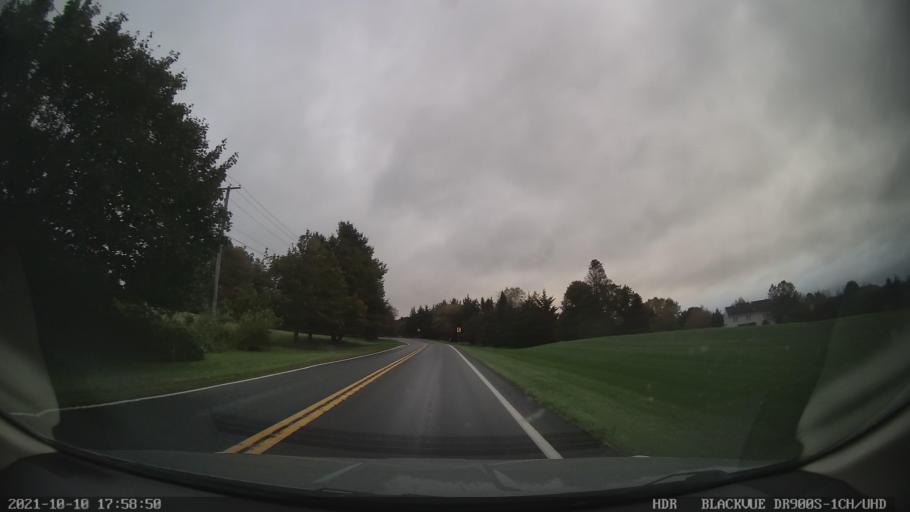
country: US
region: Pennsylvania
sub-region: Lehigh County
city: Schnecksville
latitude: 40.6358
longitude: -75.5678
